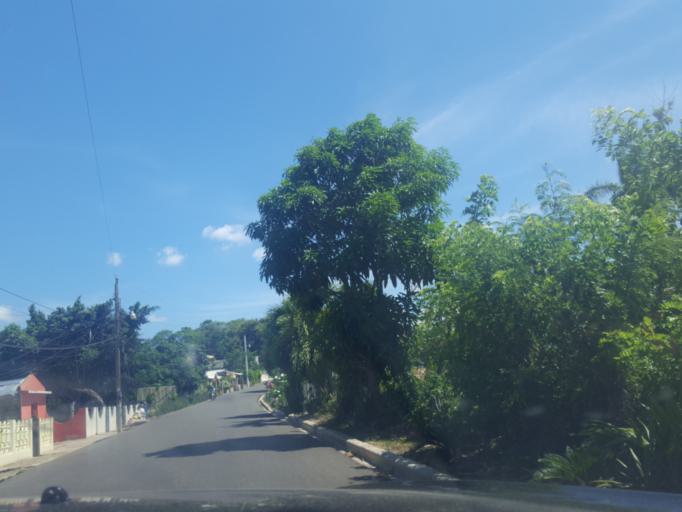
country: DO
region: Santiago
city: Licey al Medio
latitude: 19.3839
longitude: -70.6503
